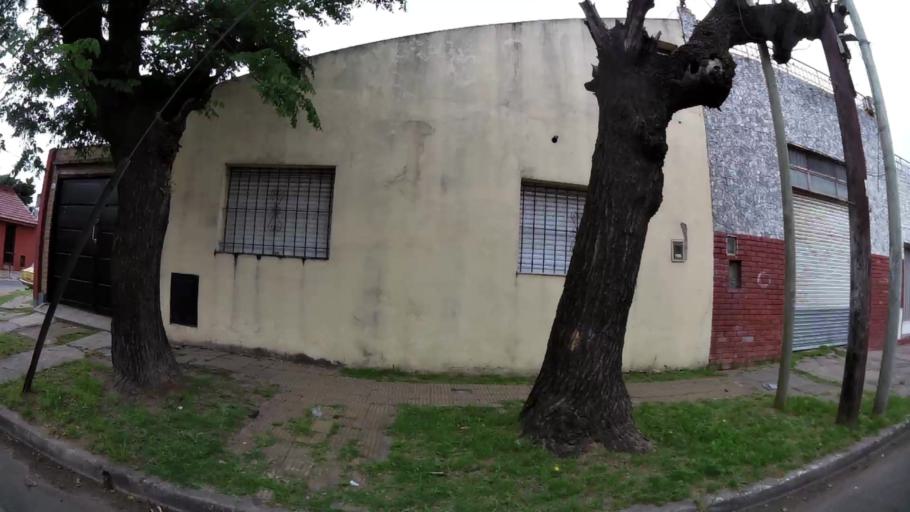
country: AR
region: Buenos Aires
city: San Justo
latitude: -34.6716
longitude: -58.5178
